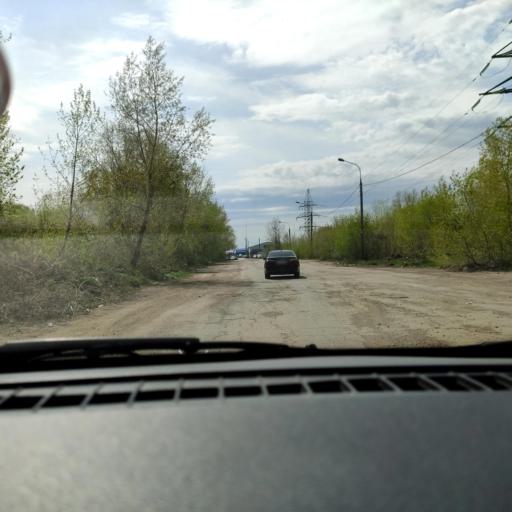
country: RU
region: Samara
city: Samara
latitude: 53.1779
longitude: 50.1243
